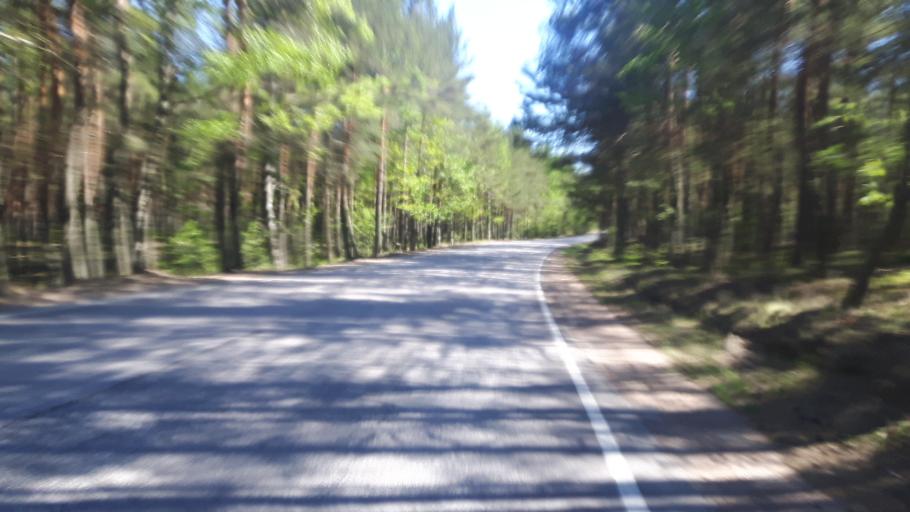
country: RU
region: Leningrad
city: Glebychevo
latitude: 60.2926
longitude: 28.8681
